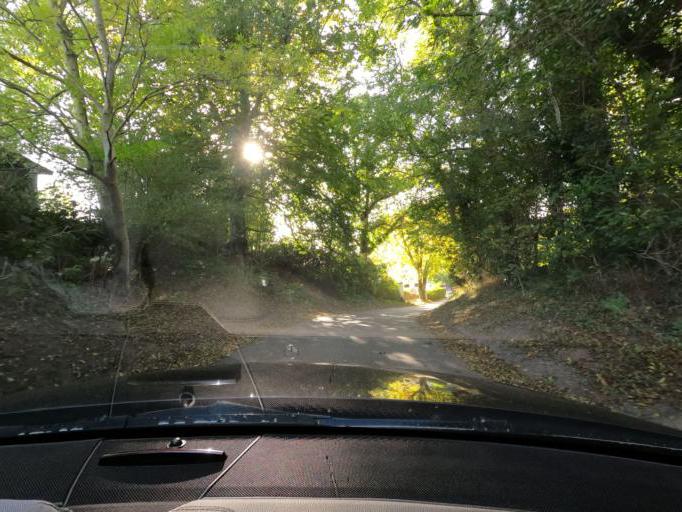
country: DK
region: South Denmark
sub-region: Sonderborg Kommune
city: Dybbol
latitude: 54.8832
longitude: 9.7264
